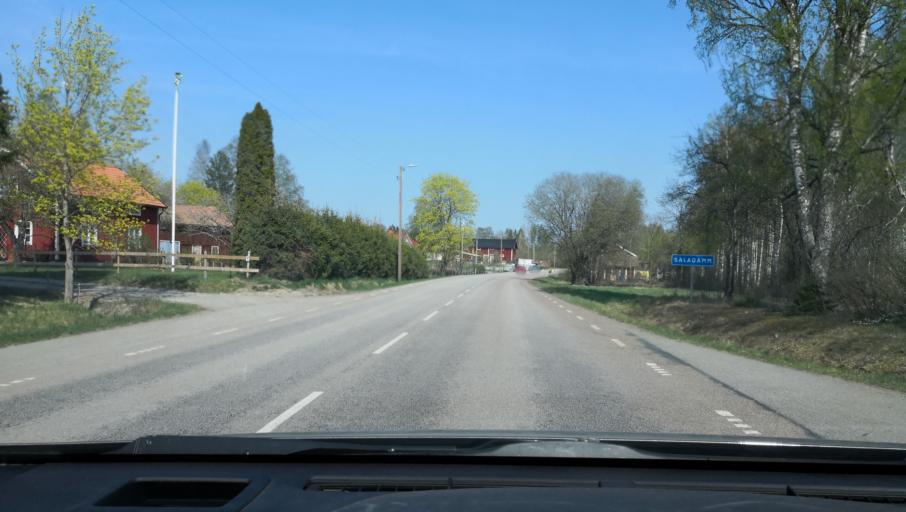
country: SE
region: Vaestmanland
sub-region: Sala Kommun
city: Sala
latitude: 59.9798
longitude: 16.6344
